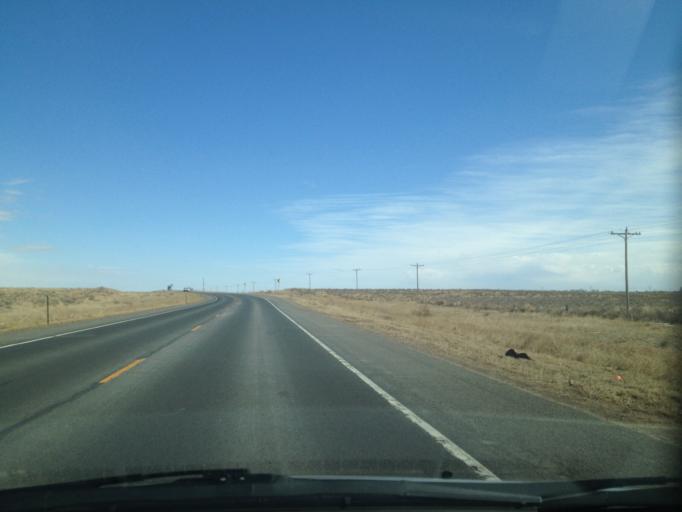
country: US
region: Colorado
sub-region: Weld County
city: Kersey
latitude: 40.2915
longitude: -104.2742
